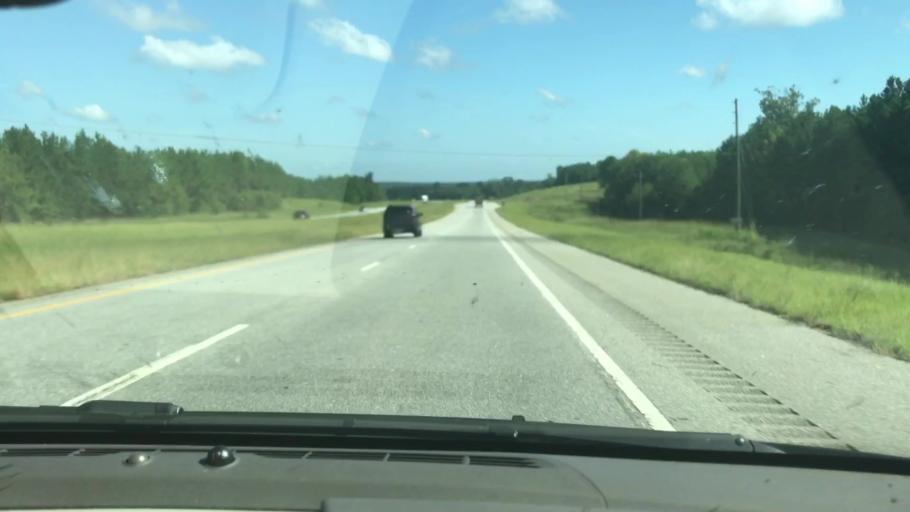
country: US
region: Alabama
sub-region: Barbour County
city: Eufaula
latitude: 32.1622
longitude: -85.1774
